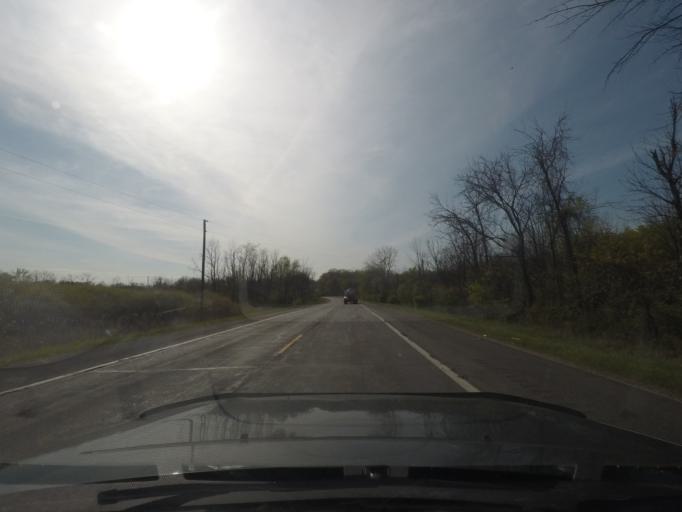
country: US
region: Michigan
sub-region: Berrien County
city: Buchanan
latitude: 41.7967
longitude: -86.4562
